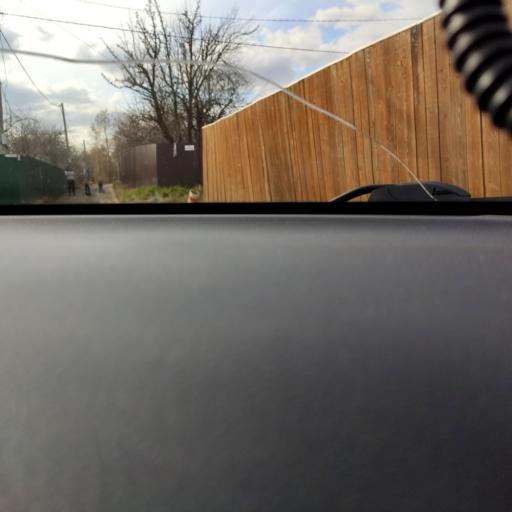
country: RU
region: Tatarstan
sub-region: Gorod Kazan'
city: Kazan
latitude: 55.8876
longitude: 49.0670
